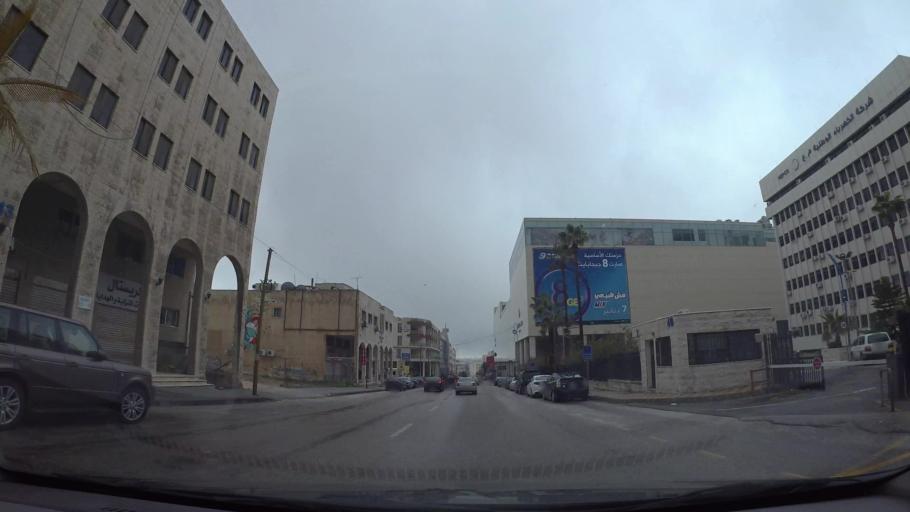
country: JO
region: Amman
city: Wadi as Sir
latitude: 31.9589
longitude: 35.8638
